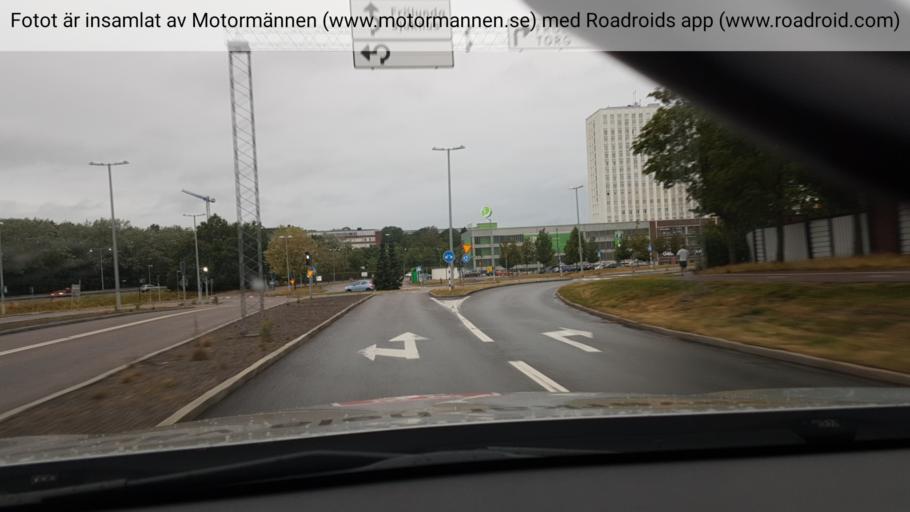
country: SE
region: Vaestra Goetaland
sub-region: Goteborg
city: Majorna
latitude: 57.6495
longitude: 11.9165
